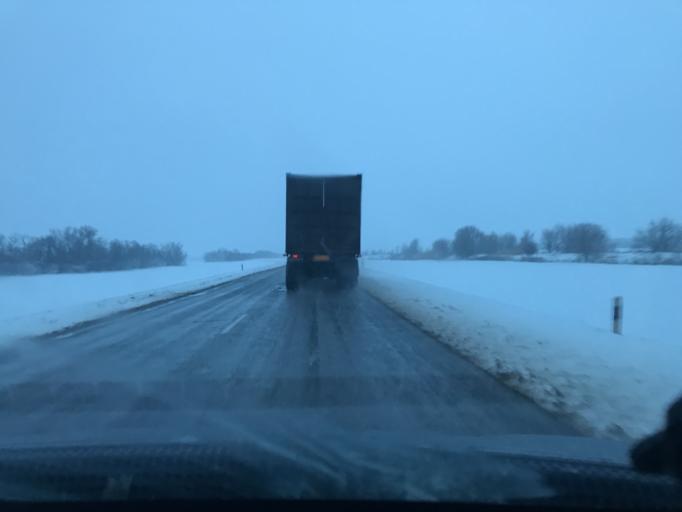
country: RU
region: Rostov
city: Letnik
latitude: 46.0503
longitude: 41.2109
